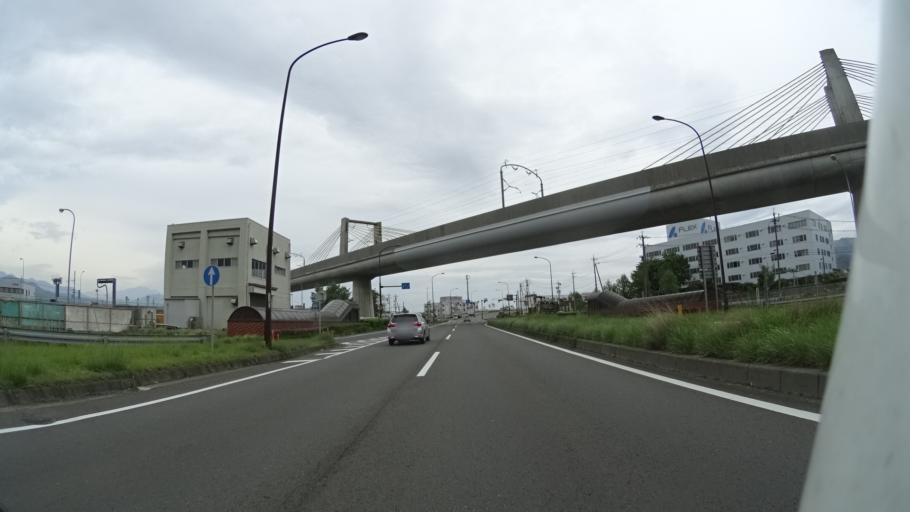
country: JP
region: Nagano
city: Nagano-shi
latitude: 36.5474
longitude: 138.1299
